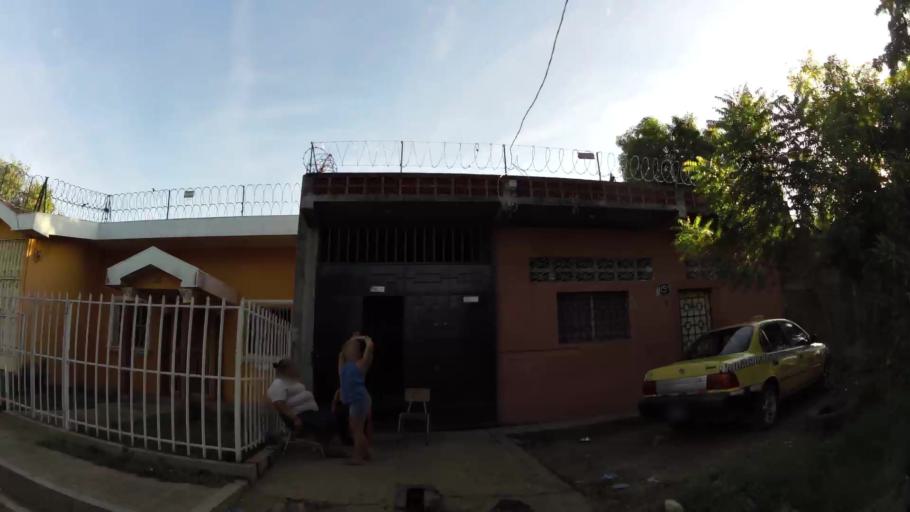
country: SV
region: San Miguel
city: San Miguel
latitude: 13.4629
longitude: -88.1699
